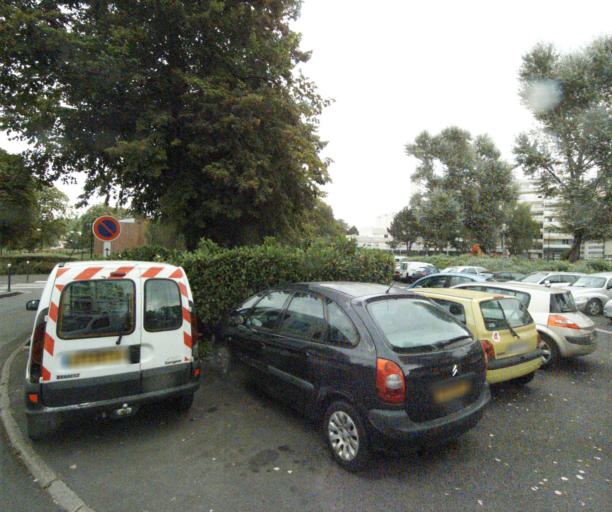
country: FR
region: Nord-Pas-de-Calais
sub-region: Departement du Nord
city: Mons-en-Baroeul
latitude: 50.6264
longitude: 3.1306
